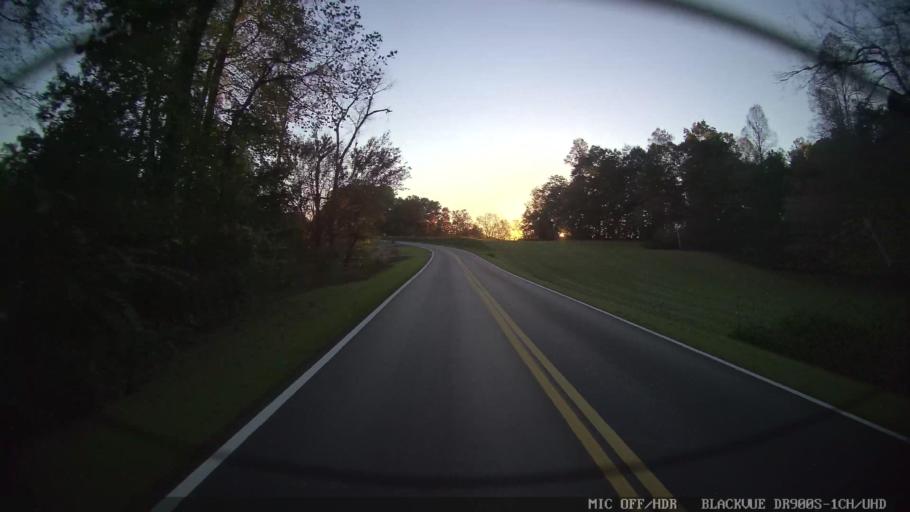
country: US
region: Georgia
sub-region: Union County
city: Blairsville
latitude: 34.8516
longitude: -83.9174
